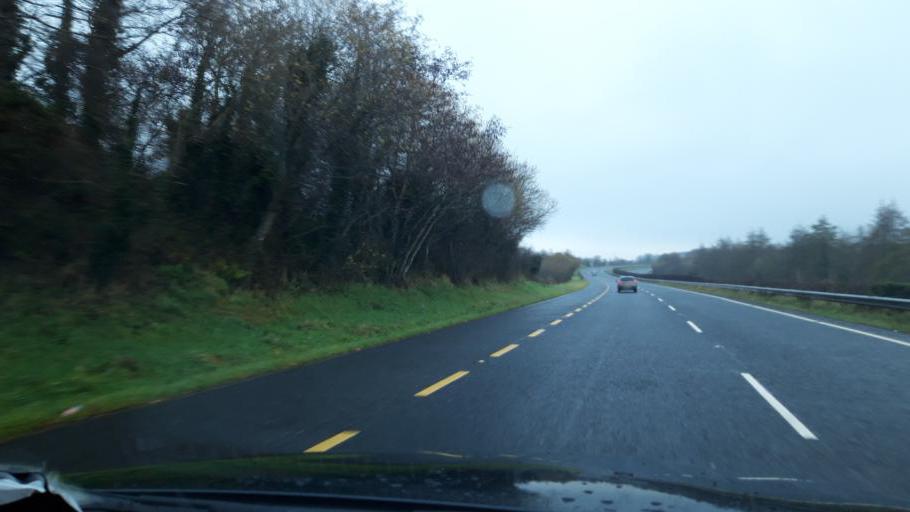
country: IE
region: Ulster
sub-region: County Donegal
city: Letterkenny
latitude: 54.9480
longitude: -7.6712
